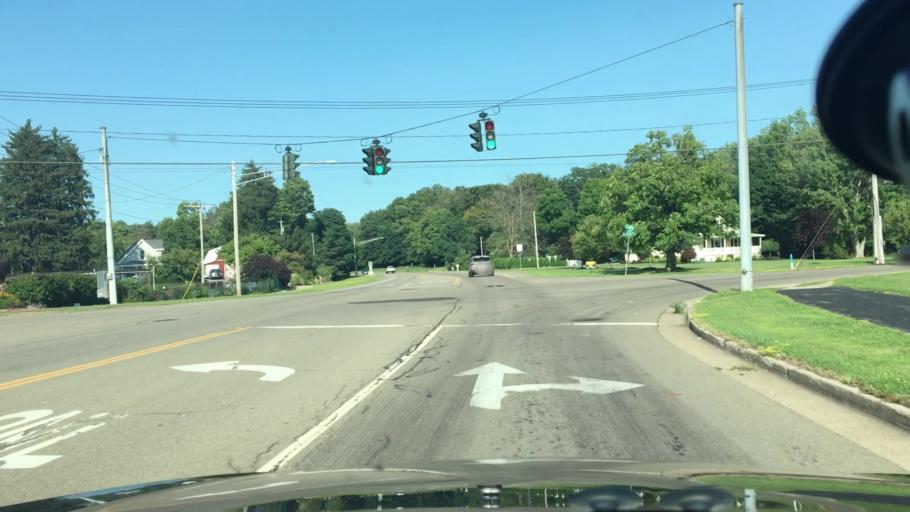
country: US
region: New York
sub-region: Erie County
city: Angola
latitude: 42.6501
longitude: -79.0337
